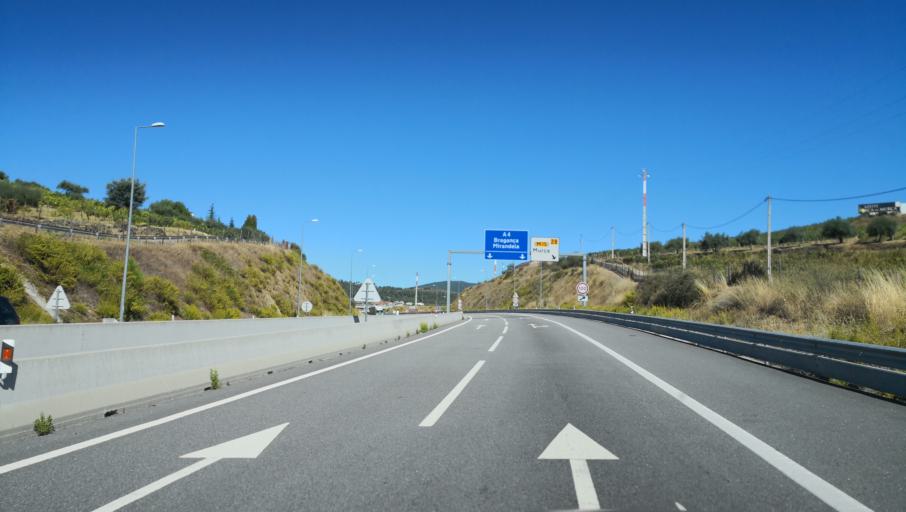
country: PT
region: Vila Real
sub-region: Murca
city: Murca
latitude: 41.3938
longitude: -7.4473
